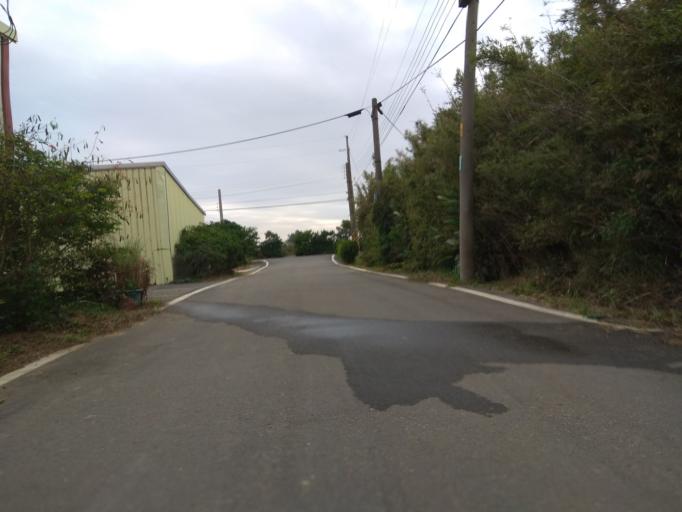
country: TW
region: Taiwan
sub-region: Hsinchu
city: Zhubei
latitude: 24.9736
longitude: 121.0376
